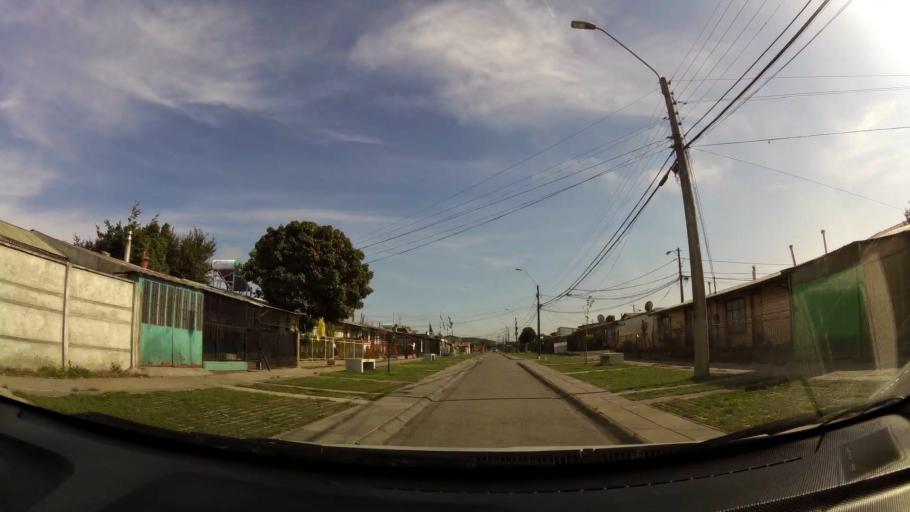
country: CL
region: Biobio
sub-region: Provincia de Concepcion
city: Talcahuano
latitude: -36.7848
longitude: -73.1143
